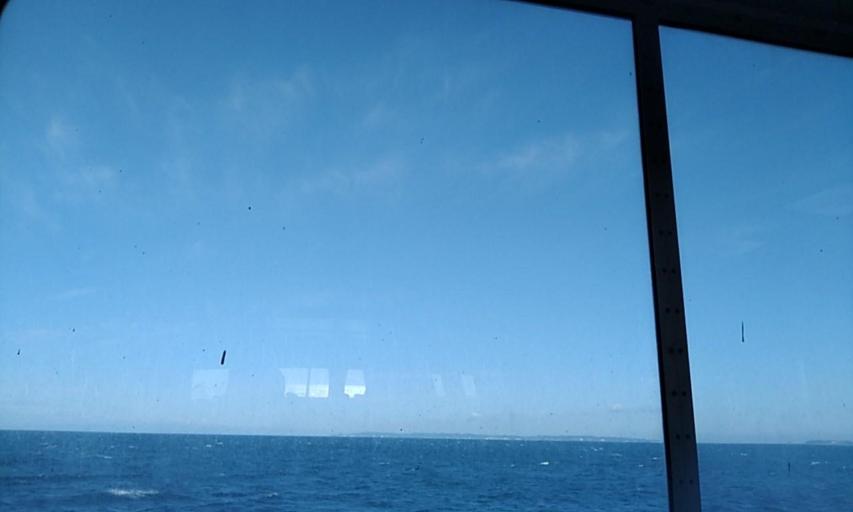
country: JP
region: Aichi
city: Toyohama
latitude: 34.5812
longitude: 136.9925
